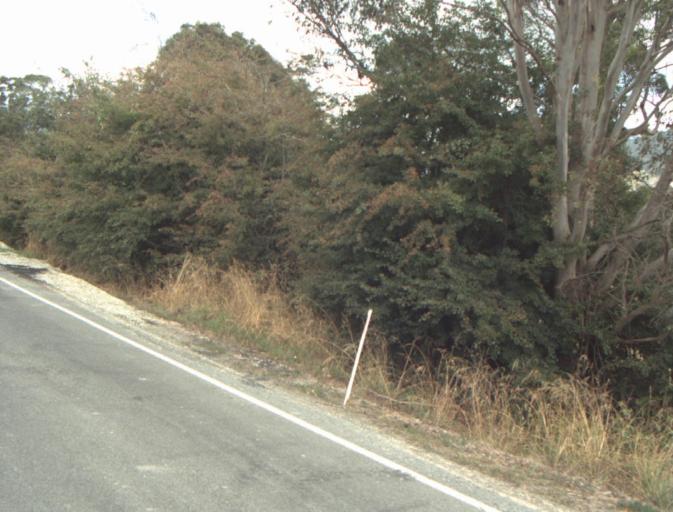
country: AU
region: Tasmania
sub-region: Launceston
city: Mayfield
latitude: -41.2342
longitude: 147.2120
